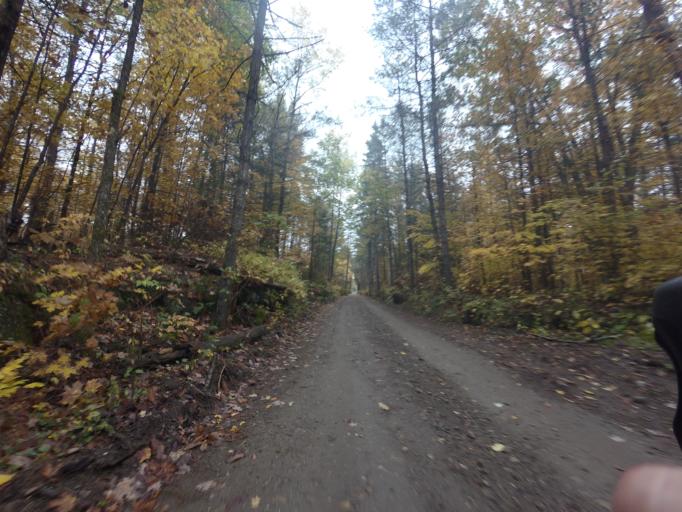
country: CA
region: Ontario
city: Renfrew
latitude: 45.1835
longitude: -76.6850
